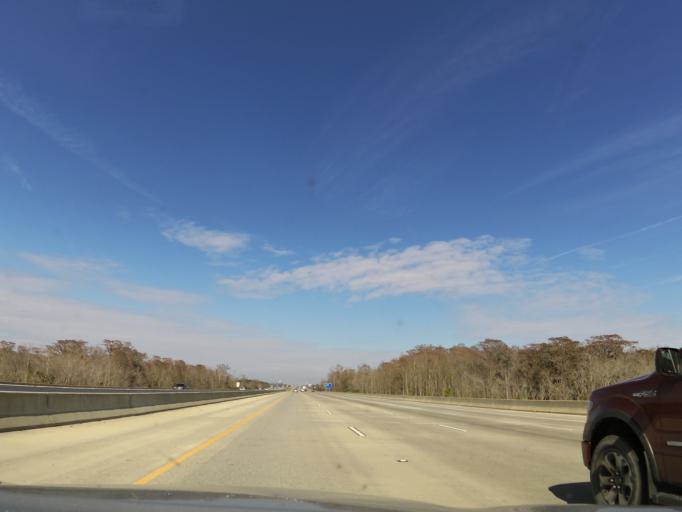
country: US
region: Georgia
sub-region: McIntosh County
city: Darien
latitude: 31.3650
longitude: -81.4573
